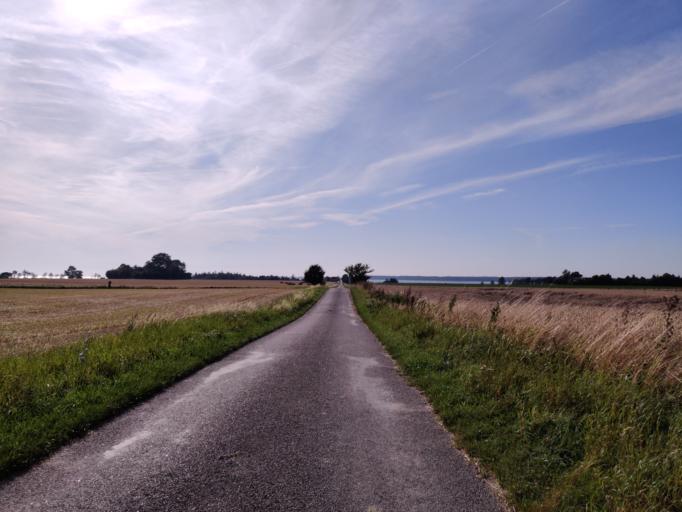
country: DK
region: Zealand
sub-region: Guldborgsund Kommune
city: Nykobing Falster
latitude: 54.6602
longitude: 11.8822
